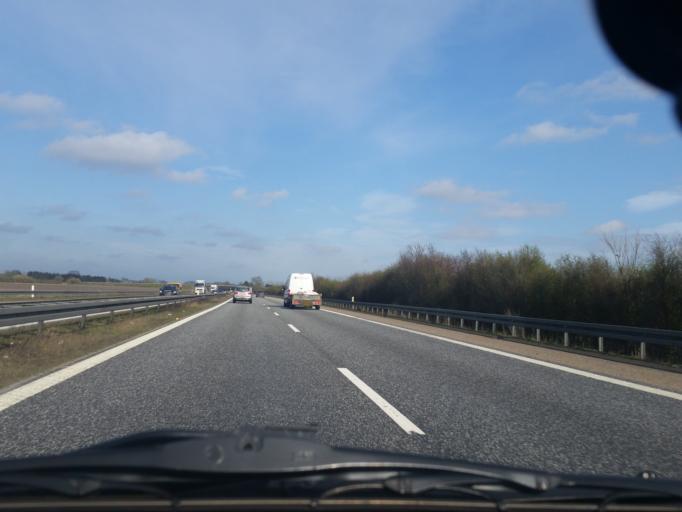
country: DK
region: Zealand
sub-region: Soro Kommune
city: Frederiksberg
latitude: 55.4475
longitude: 11.6709
